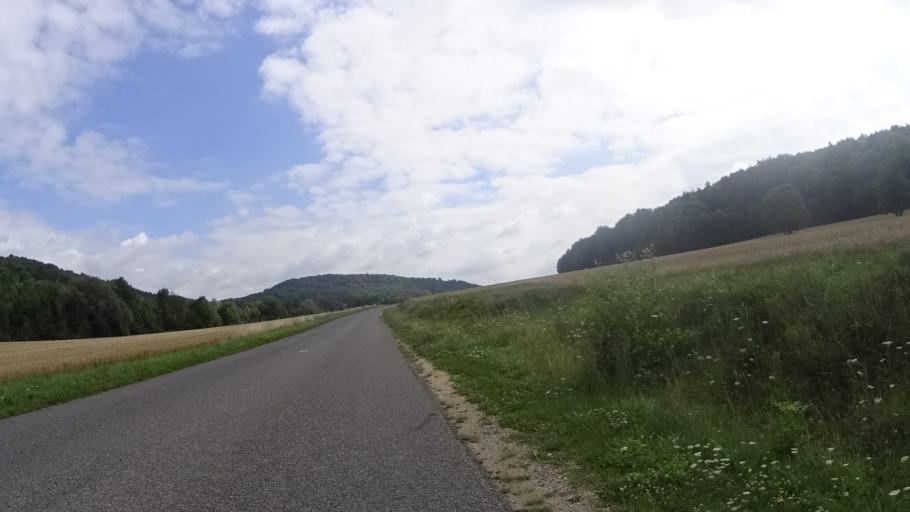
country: FR
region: Lorraine
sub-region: Departement de la Meuse
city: Velaines
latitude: 48.7154
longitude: 5.3098
